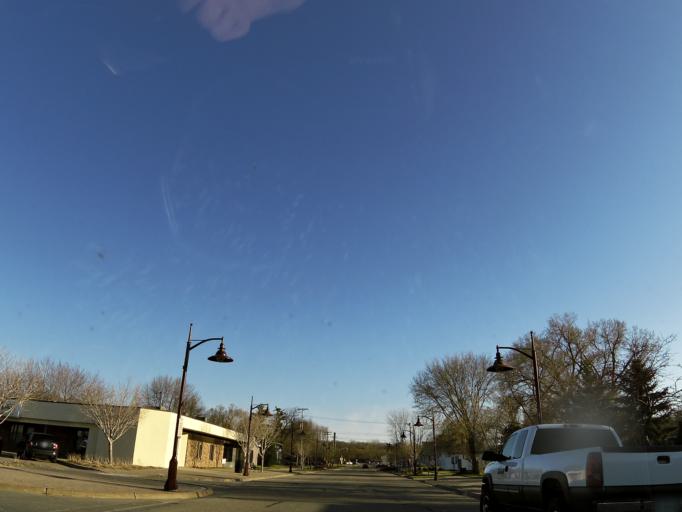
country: US
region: Minnesota
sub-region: Scott County
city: Savage
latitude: 44.7774
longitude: -93.3419
